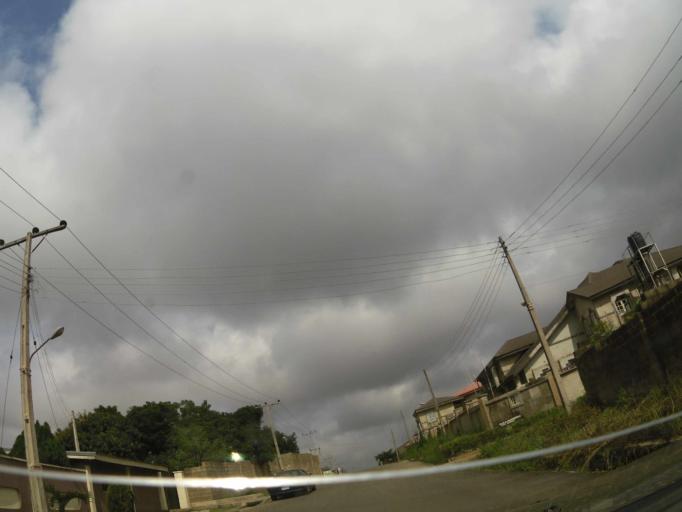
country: NG
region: Oyo
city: Ibadan
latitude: 7.4367
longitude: 3.9574
